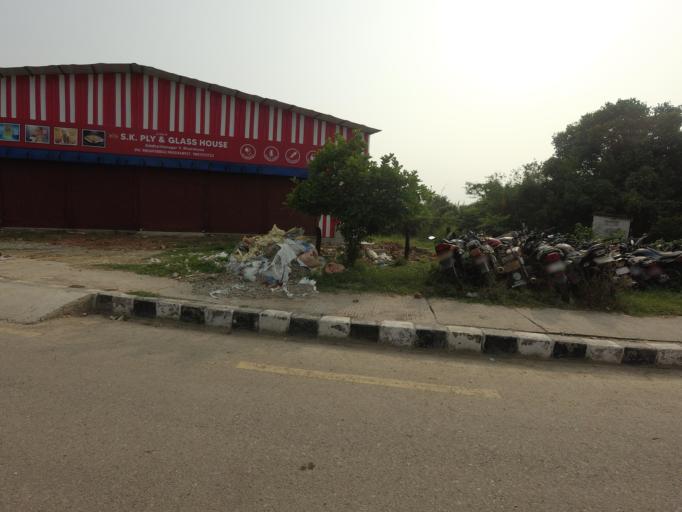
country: NP
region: Western Region
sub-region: Lumbini Zone
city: Bhairahawa
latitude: 27.5261
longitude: 83.4585
